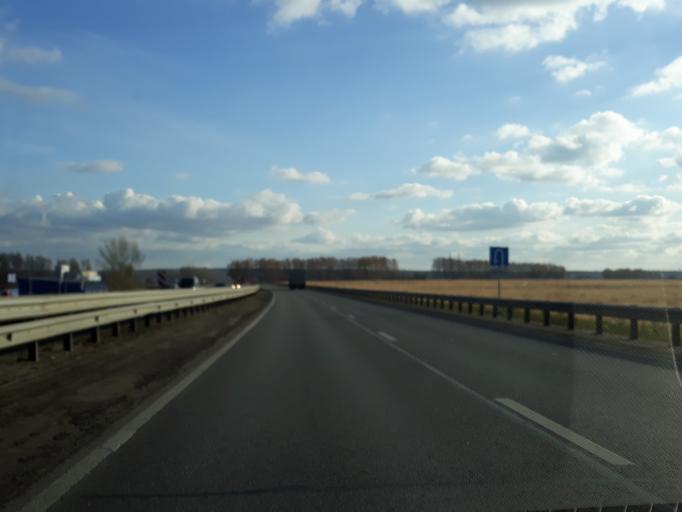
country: RU
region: Nizjnij Novgorod
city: Afonino
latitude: 56.2143
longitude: 44.0796
